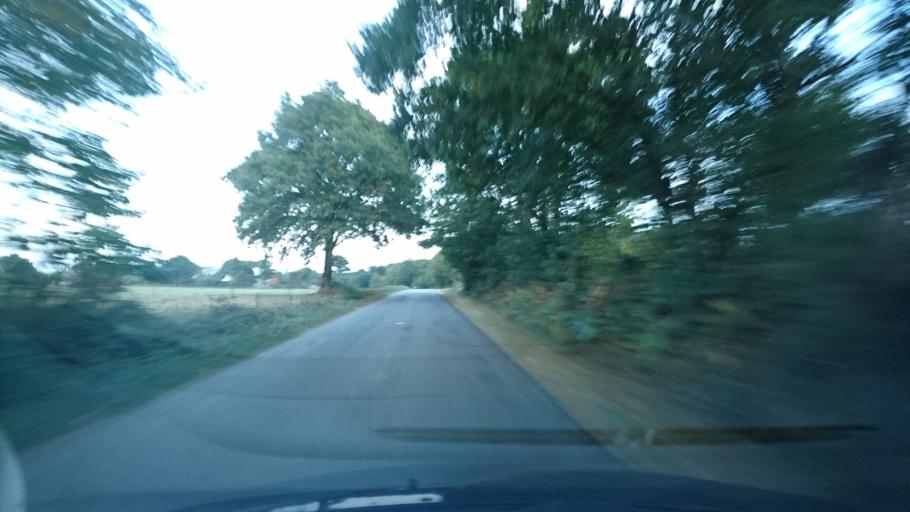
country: FR
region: Brittany
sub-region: Departement d'Ille-et-Vilaine
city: Pipriac
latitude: 47.8254
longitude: -1.9789
